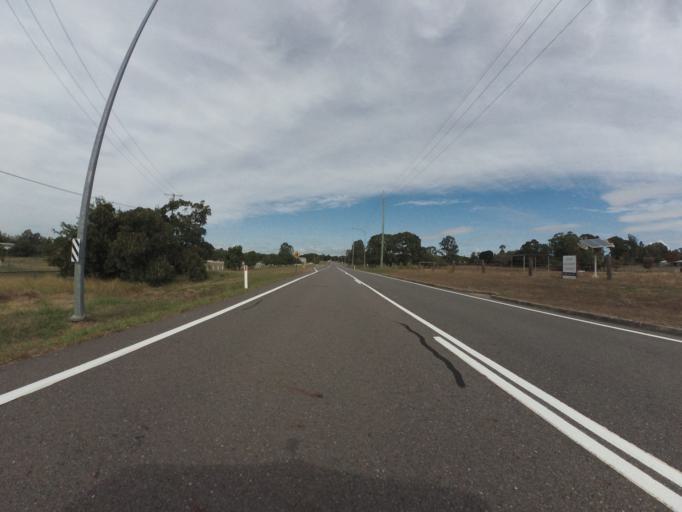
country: AU
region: Queensland
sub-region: Brisbane
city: Moggill
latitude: -27.5900
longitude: 152.8605
